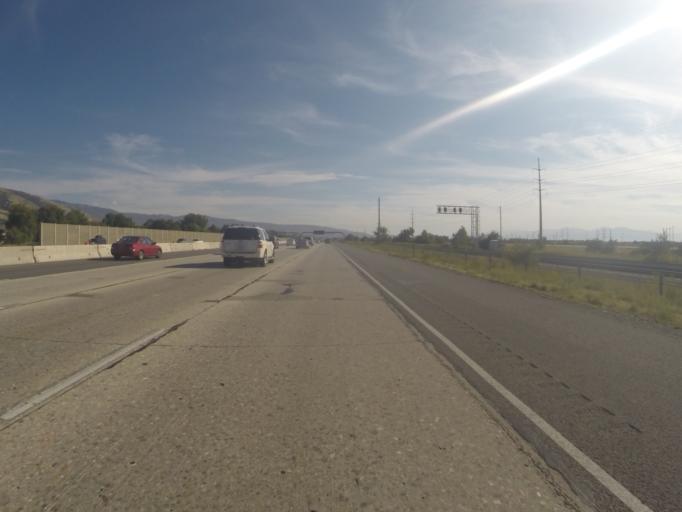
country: US
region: Utah
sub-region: Davis County
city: Farmington
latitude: 40.9495
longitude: -111.8915
